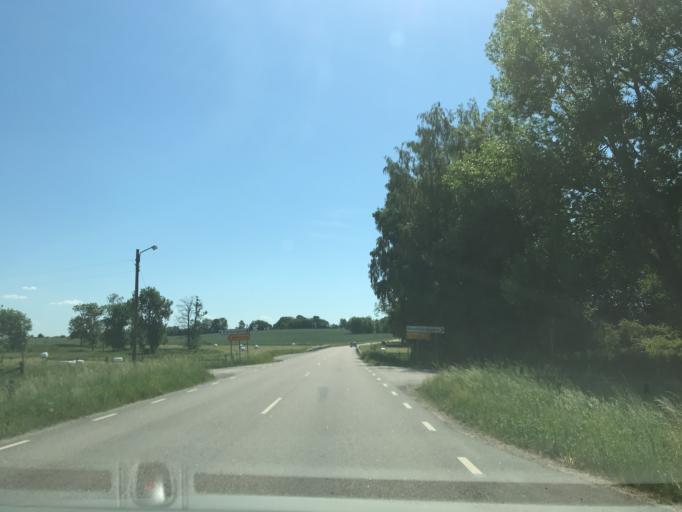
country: SE
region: Vaestra Goetaland
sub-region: Gotene Kommun
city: Kallby
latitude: 58.5142
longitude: 13.3180
